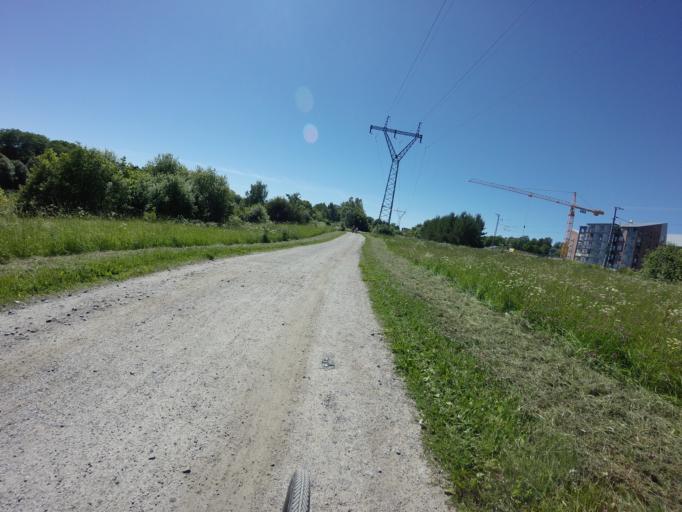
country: FI
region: Varsinais-Suomi
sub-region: Turku
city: Turku
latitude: 60.4636
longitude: 22.2818
